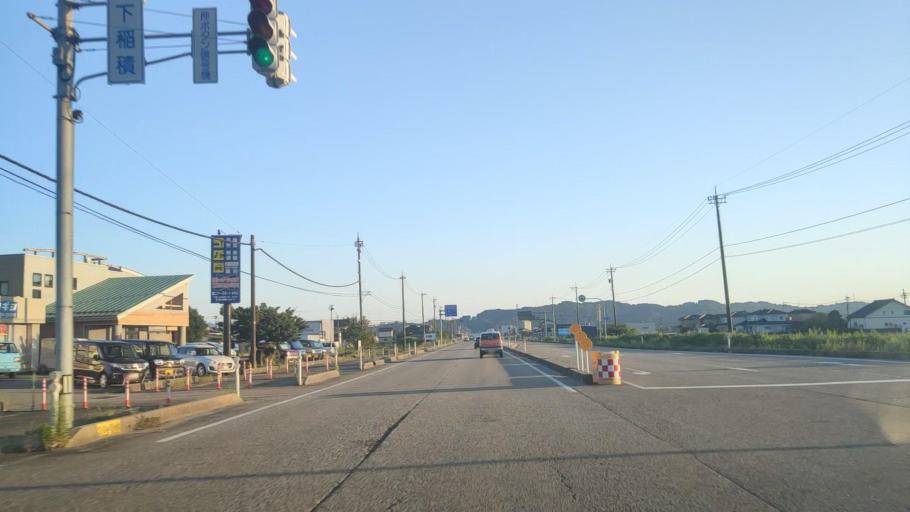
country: JP
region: Toyama
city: Himi
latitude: 36.8744
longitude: 136.9751
